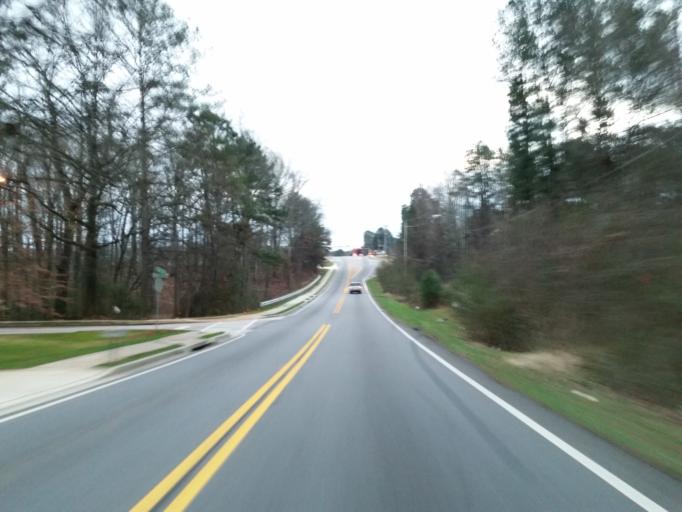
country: US
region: Georgia
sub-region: Cobb County
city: Mableton
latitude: 33.8605
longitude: -84.5773
